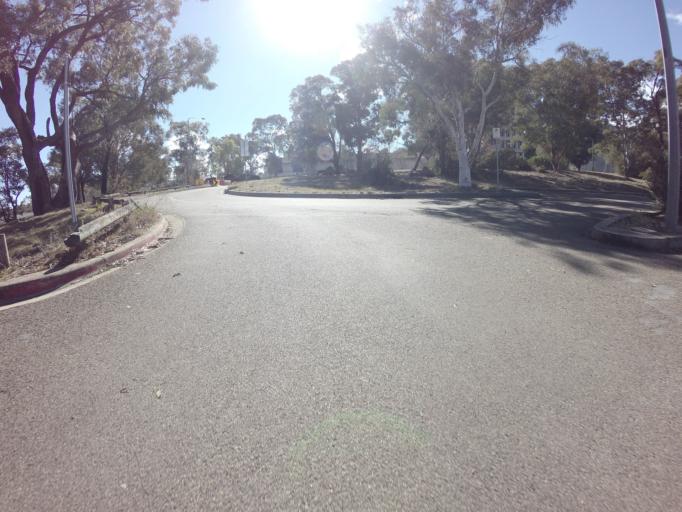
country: AU
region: Australian Capital Territory
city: Canberra
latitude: -35.2946
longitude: 149.1470
